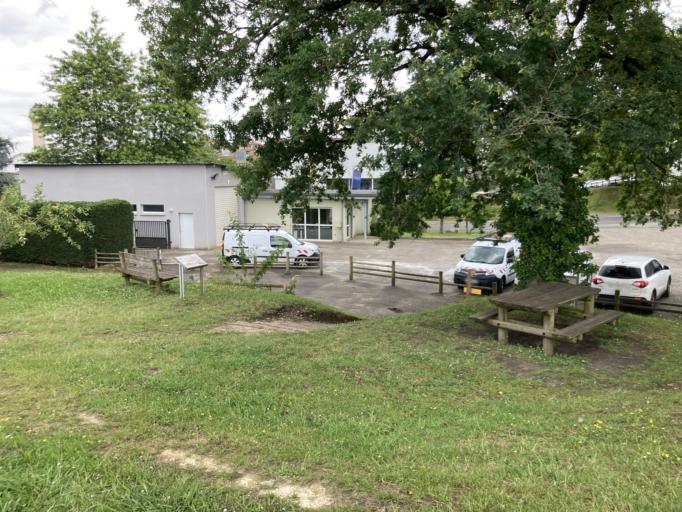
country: FR
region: Aquitaine
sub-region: Departement des Landes
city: Mugron
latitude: 43.7479
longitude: -0.7508
